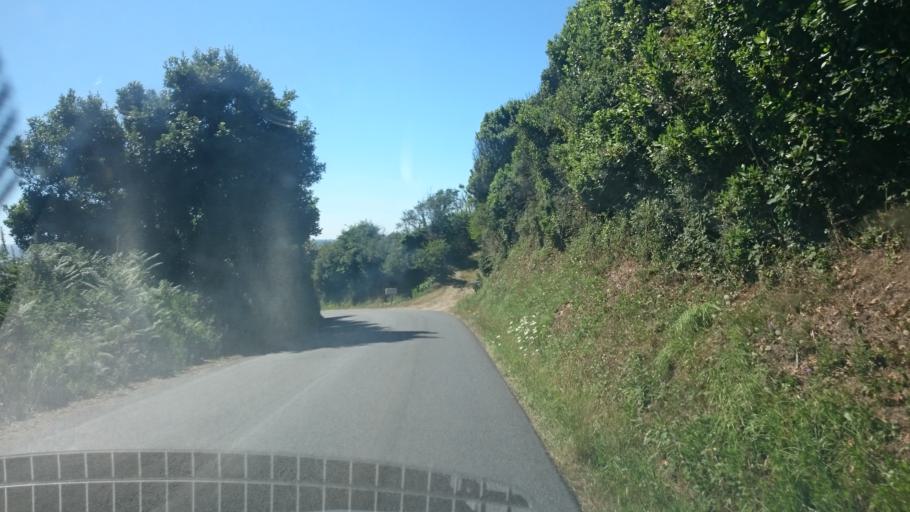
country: FR
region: Lower Normandy
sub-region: Departement de la Manche
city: Flamanville
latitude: 49.5073
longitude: -1.8435
